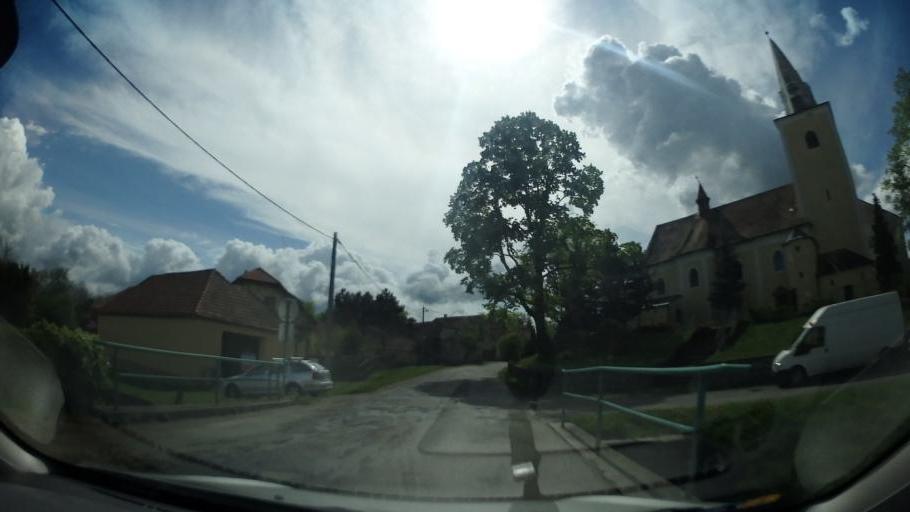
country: CZ
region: South Moravian
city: Ricany
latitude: 49.2359
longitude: 16.4045
